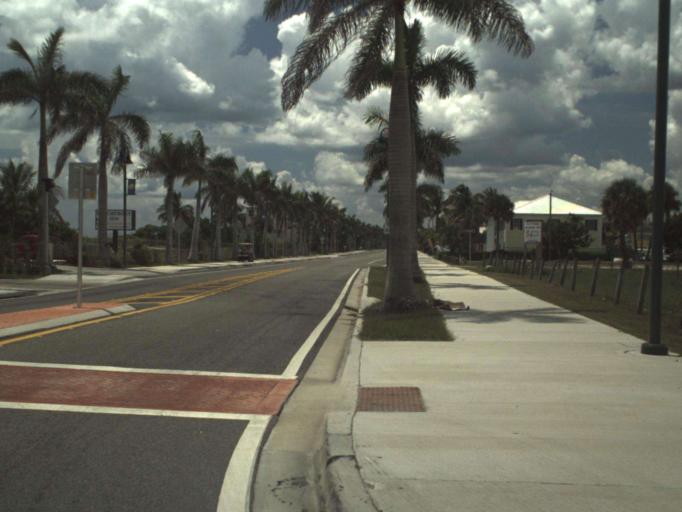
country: US
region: Florida
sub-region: Saint Lucie County
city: Fort Pierce
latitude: 27.4694
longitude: -80.2920
